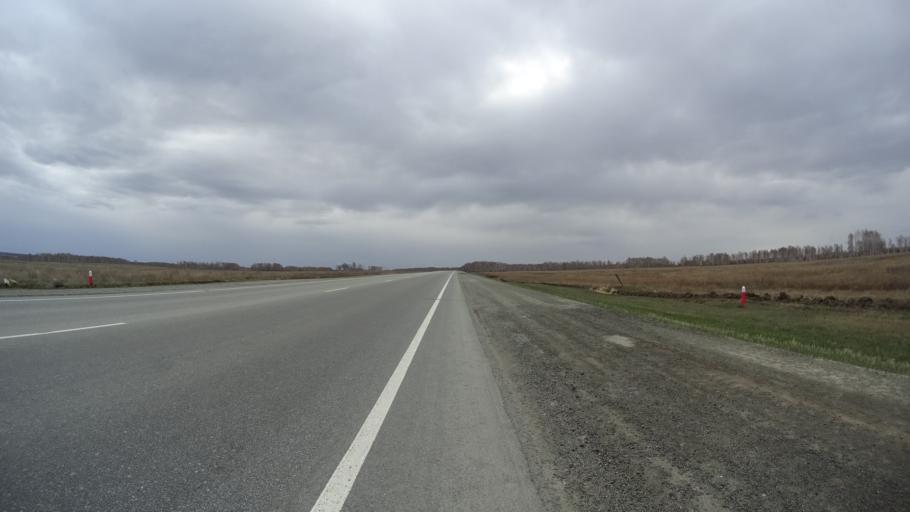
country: RU
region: Chelyabinsk
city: Yemanzhelinsk
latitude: 54.7049
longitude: 61.2558
